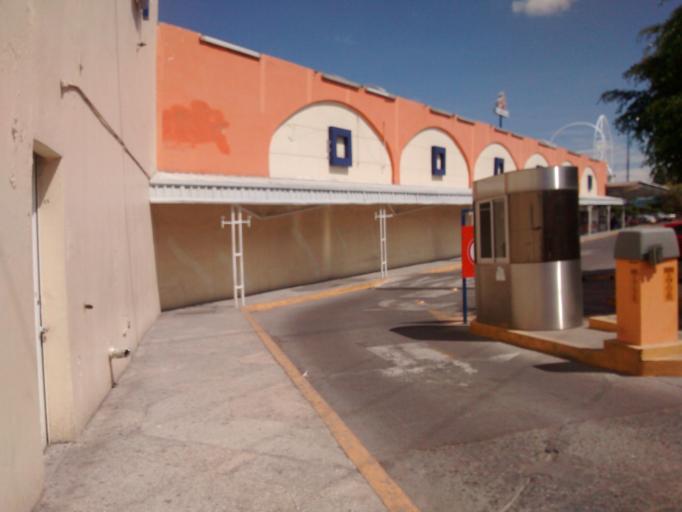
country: MX
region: Puebla
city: Tehuacan
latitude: 18.4643
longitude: -97.3870
